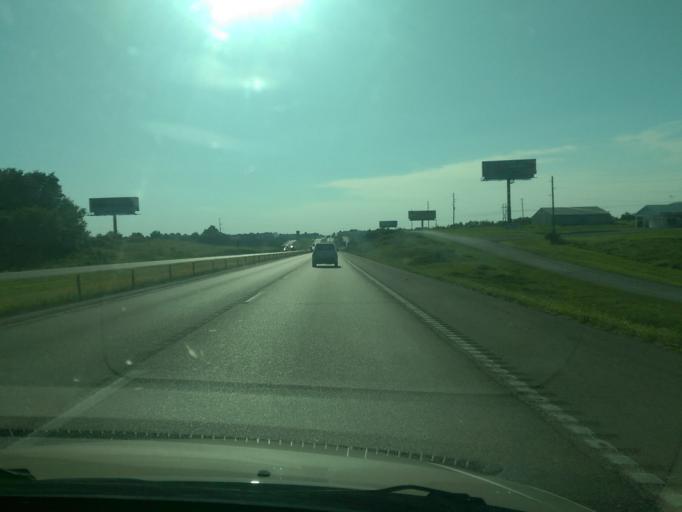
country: US
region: Missouri
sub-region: Jackson County
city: Grain Valley
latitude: 39.0252
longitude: -94.2292
